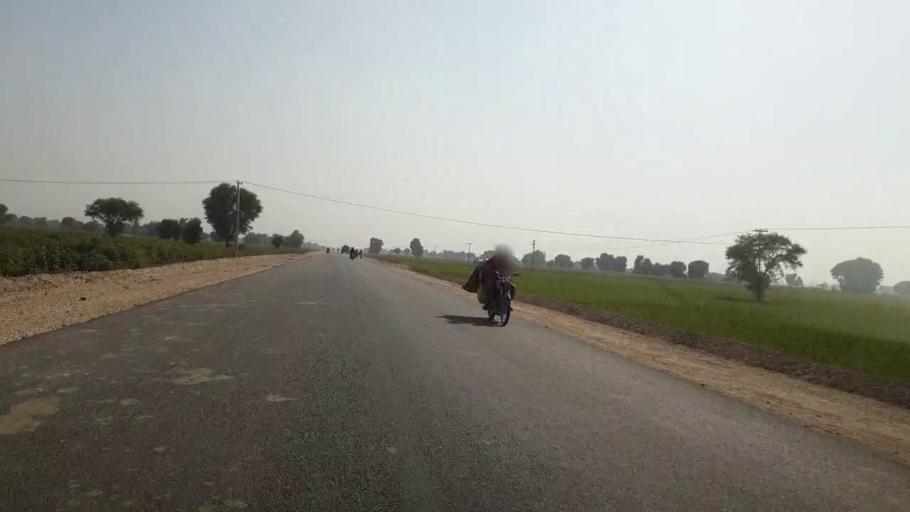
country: PK
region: Sindh
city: Dadu
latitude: 26.6733
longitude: 67.7765
